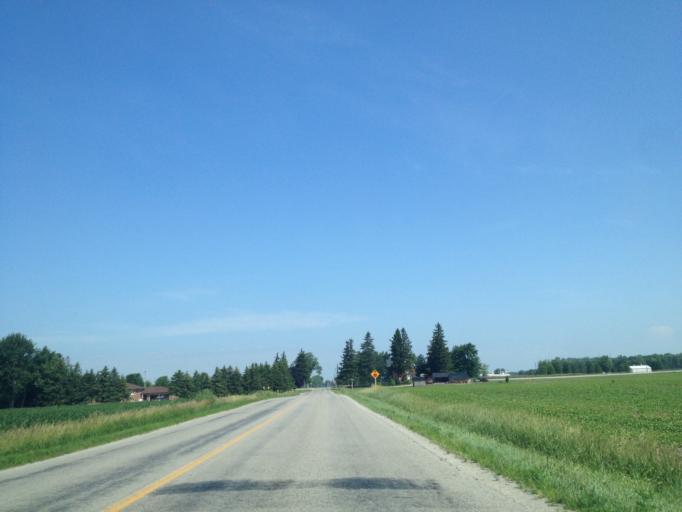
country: CA
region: Ontario
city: London
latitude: 43.1392
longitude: -81.2120
